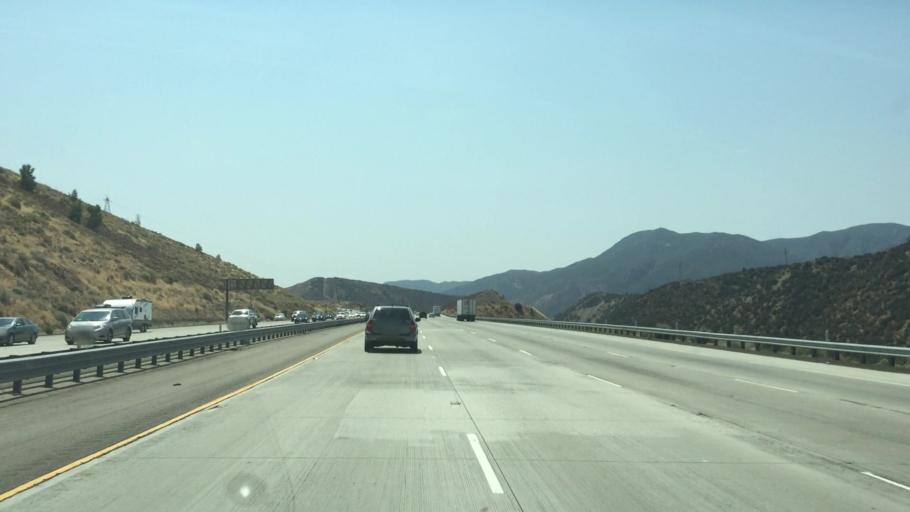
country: US
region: California
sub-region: Kern County
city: Lebec
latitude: 34.6932
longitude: -118.7897
